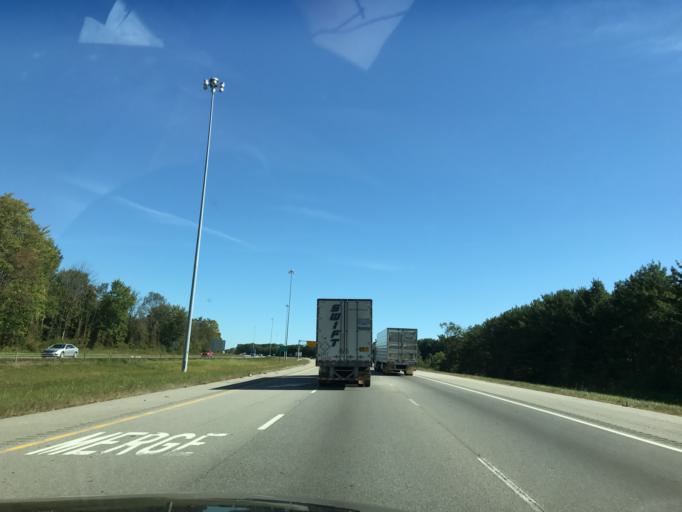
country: US
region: Ohio
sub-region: Franklin County
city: Reynoldsburg
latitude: 39.9382
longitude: -82.7705
